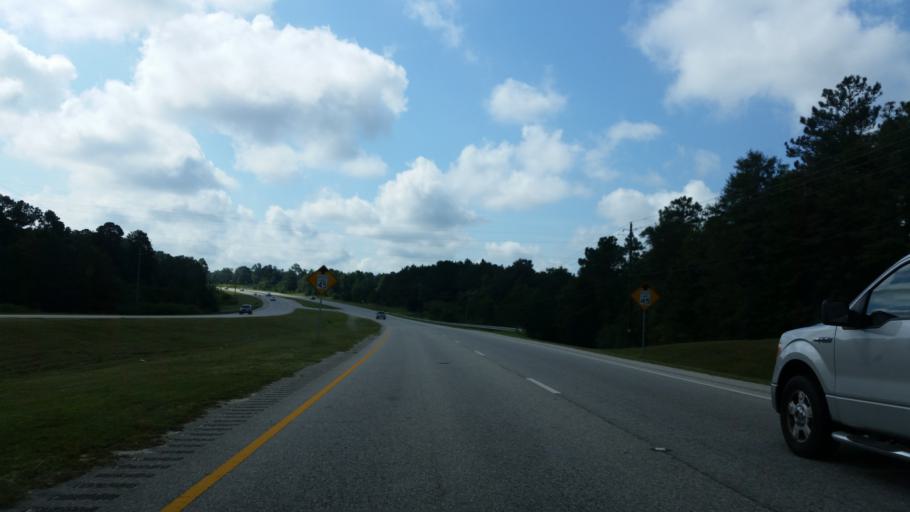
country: US
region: Alabama
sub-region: Baldwin County
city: Bay Minette
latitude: 30.9020
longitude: -87.7944
